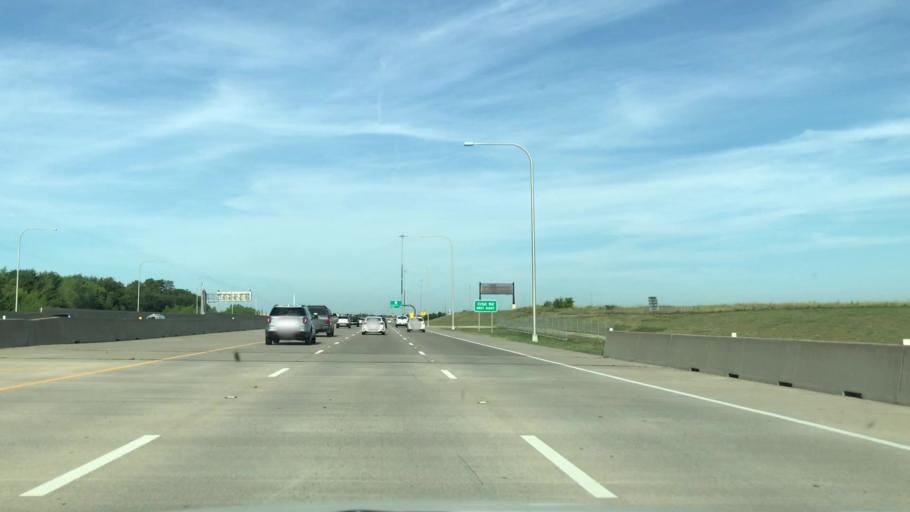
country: US
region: Texas
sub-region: Dallas County
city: Sachse
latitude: 32.9487
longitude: -96.6007
